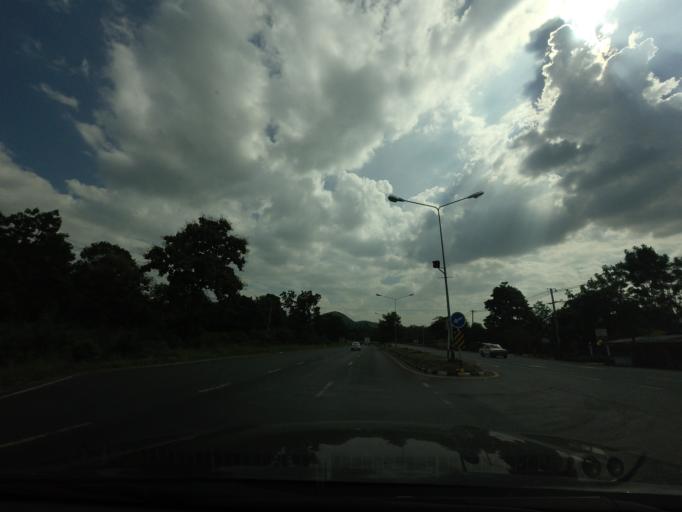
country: TH
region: Lop Buri
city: Chai Badan
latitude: 15.3100
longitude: 101.1230
